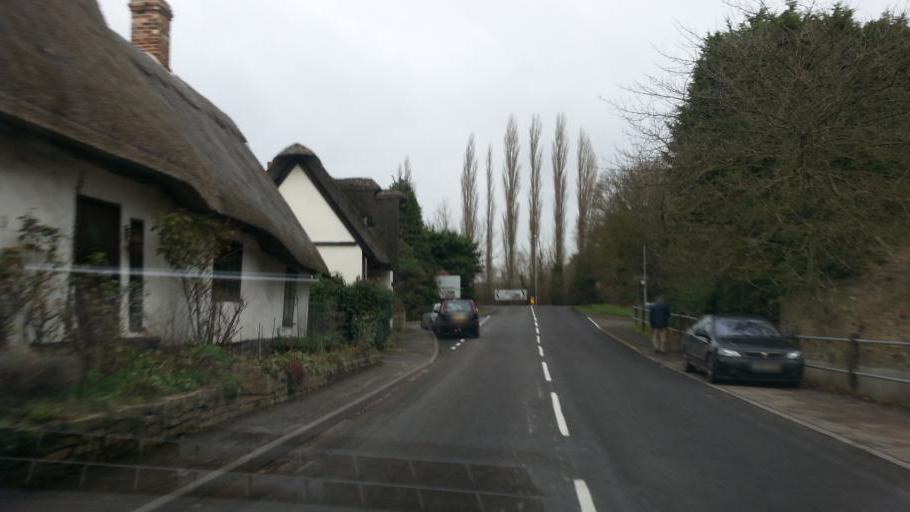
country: GB
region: England
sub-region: Cambridgeshire
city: Linton
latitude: 52.0942
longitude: 0.2751
